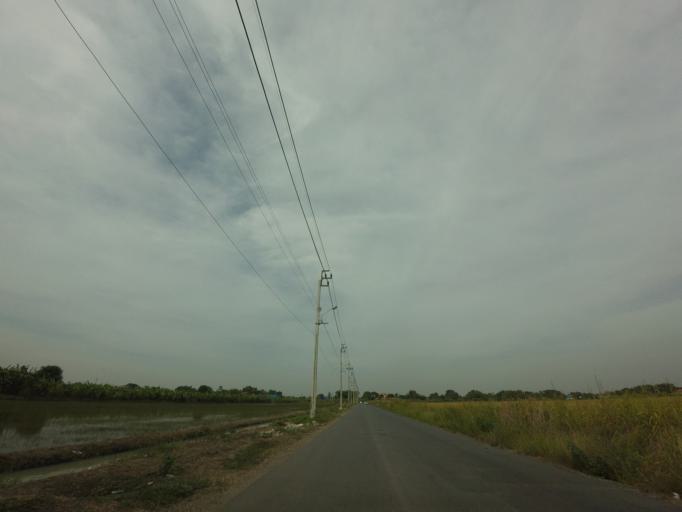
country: TH
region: Bangkok
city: Khlong Sam Wa
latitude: 13.8878
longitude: 100.7039
